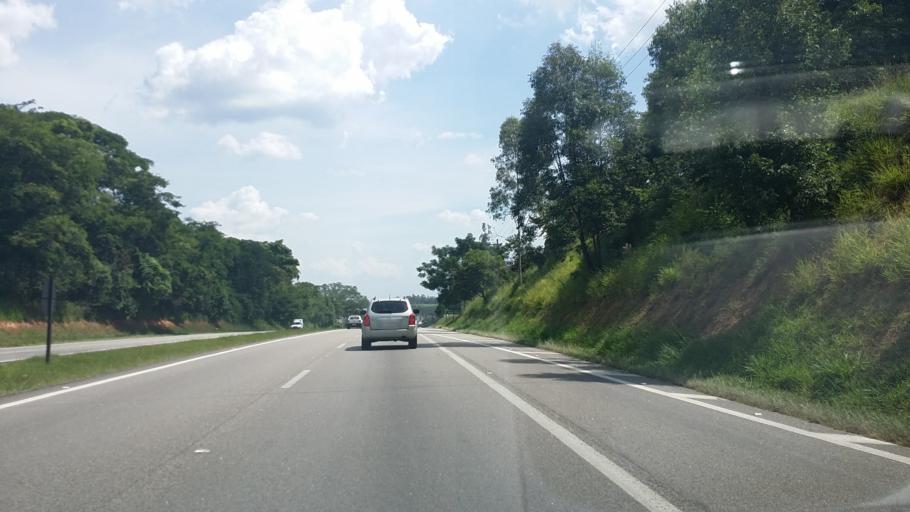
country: BR
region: Sao Paulo
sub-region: Itupeva
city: Itupeva
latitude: -23.2129
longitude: -47.0170
